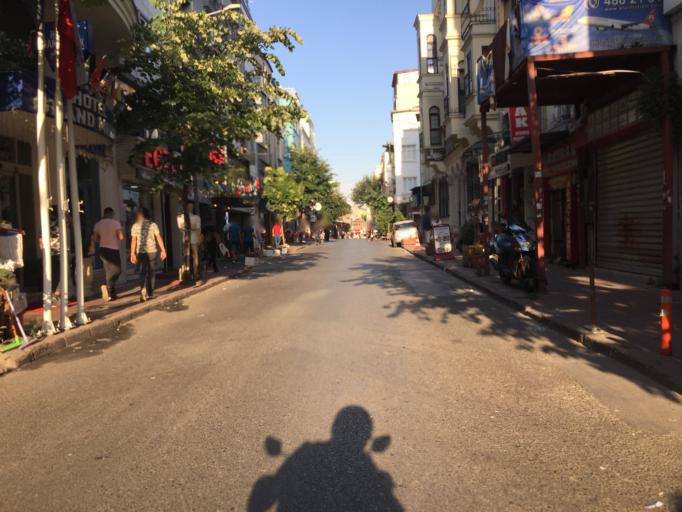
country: TR
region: Istanbul
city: Eminoenue
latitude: 41.0050
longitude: 28.9645
